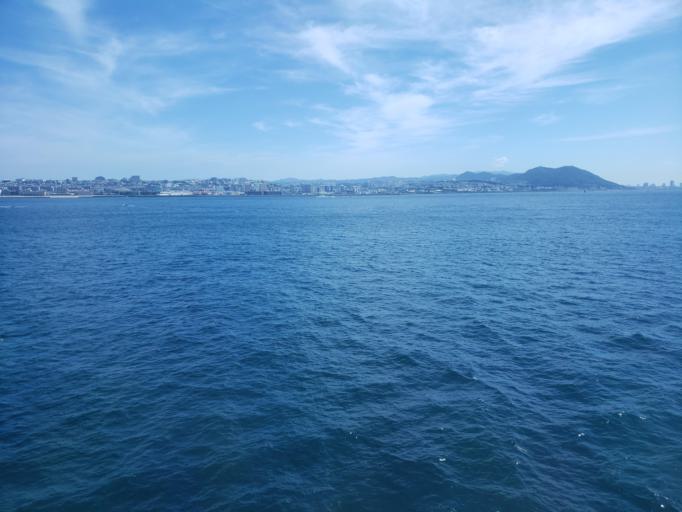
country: JP
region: Hyogo
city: Akashi
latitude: 34.6081
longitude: 135.0424
